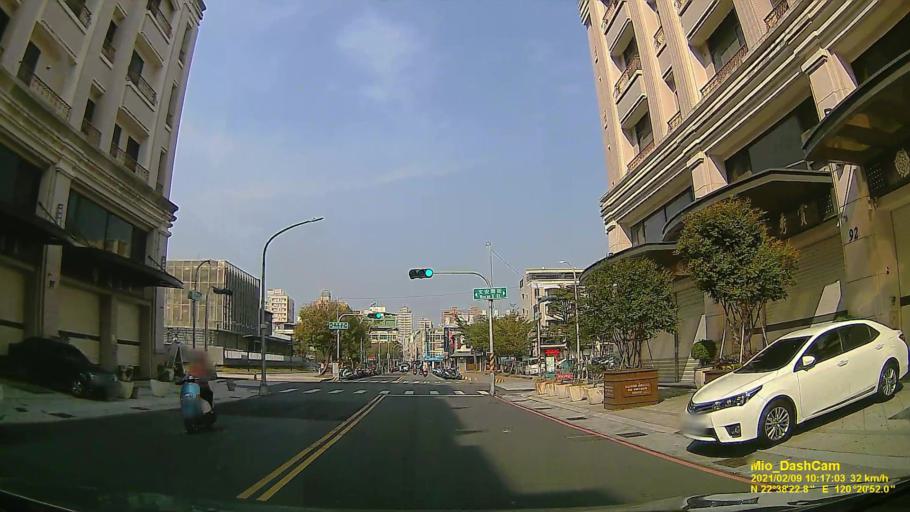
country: TW
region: Taiwan
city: Fengshan
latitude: 22.6396
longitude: 120.3479
